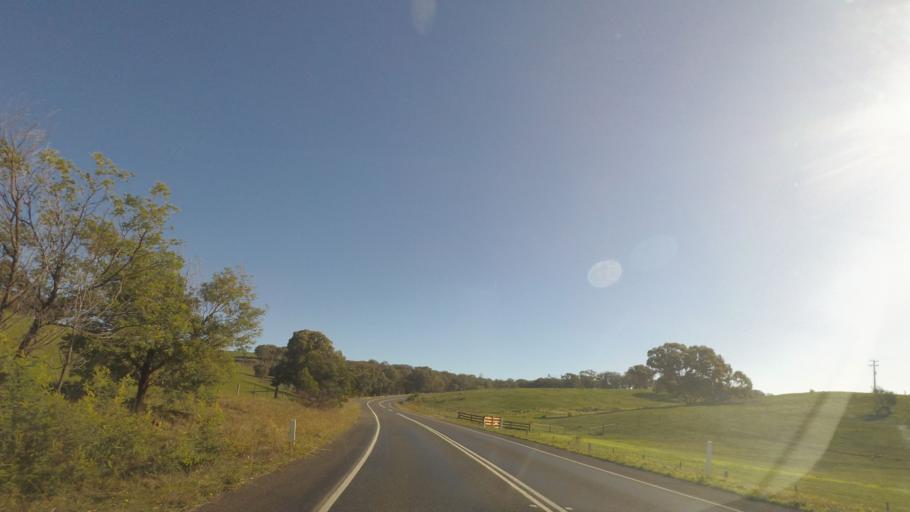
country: AU
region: Victoria
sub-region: Greater Bendigo
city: Kennington
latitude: -36.9129
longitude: 144.3316
